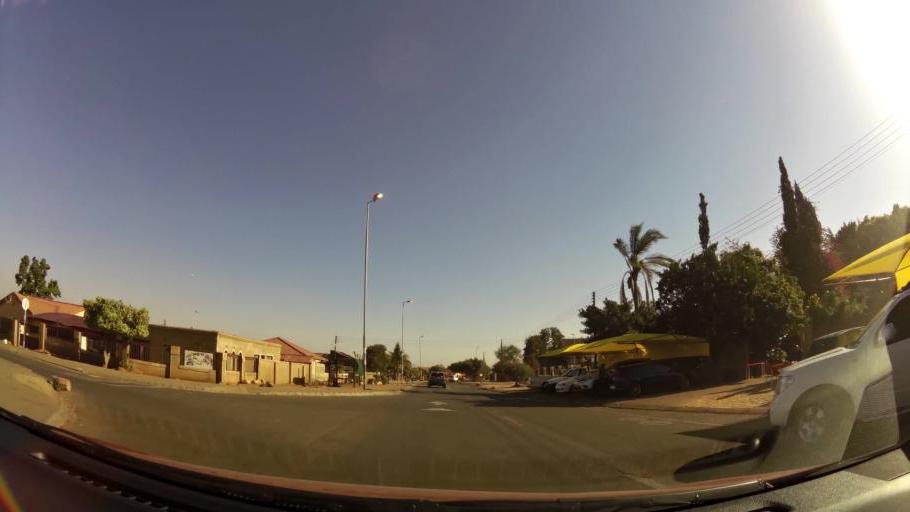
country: ZA
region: Gauteng
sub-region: City of Tshwane Metropolitan Municipality
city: Mabopane
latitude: -25.5437
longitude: 28.1015
